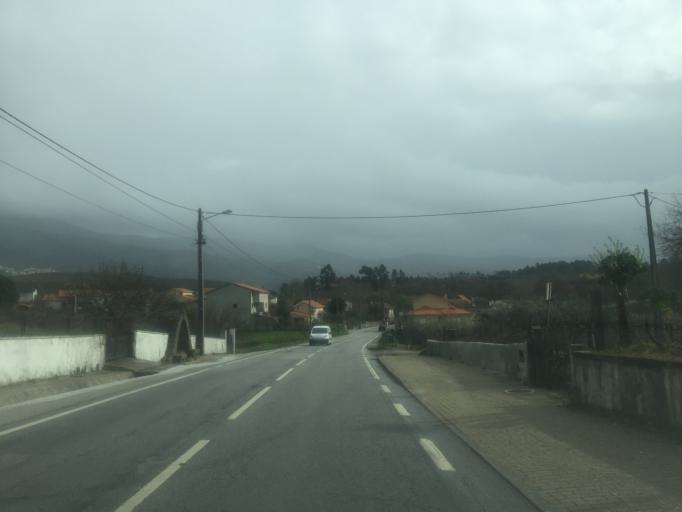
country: PT
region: Guarda
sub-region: Seia
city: Seia
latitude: 40.4003
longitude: -7.7418
